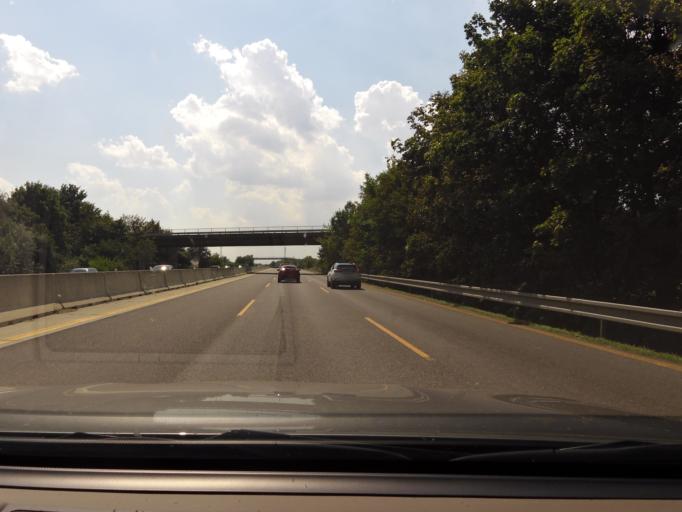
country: SK
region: Bratislavsky
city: Senec
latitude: 48.2805
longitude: 17.4727
